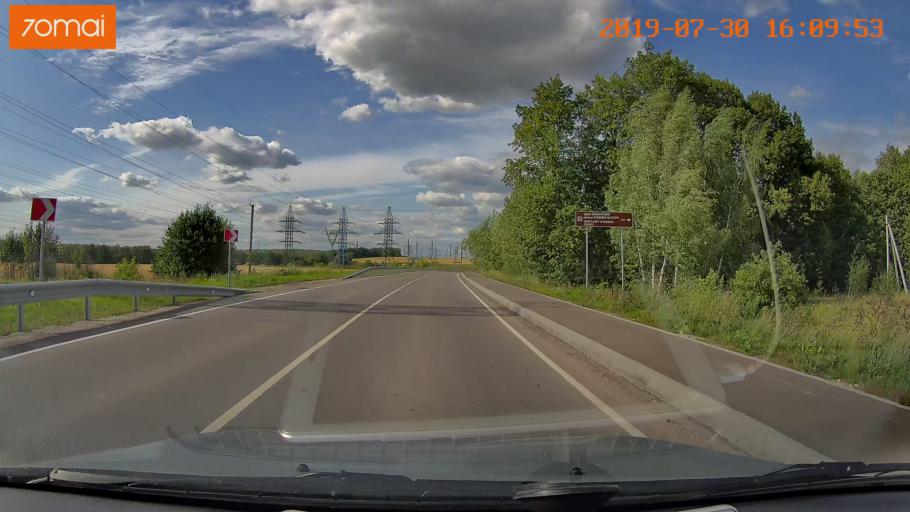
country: RU
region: Moskovskaya
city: Peski
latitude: 55.2570
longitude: 38.7159
